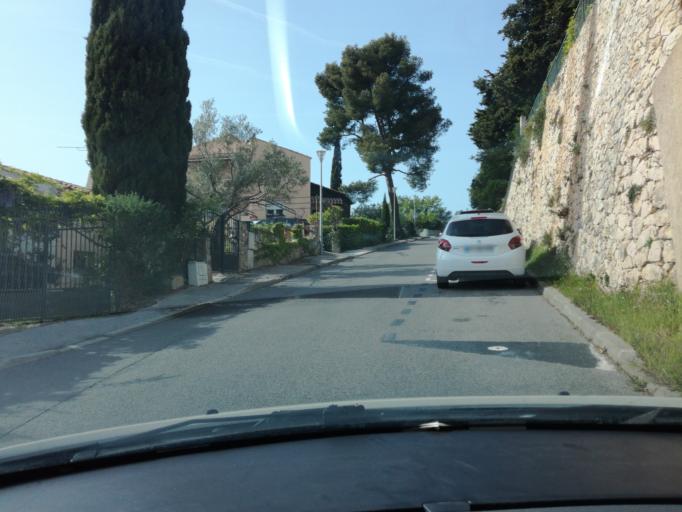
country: FR
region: Provence-Alpes-Cote d'Azur
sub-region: Departement du Var
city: Hyeres
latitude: 43.1227
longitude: 6.1227
